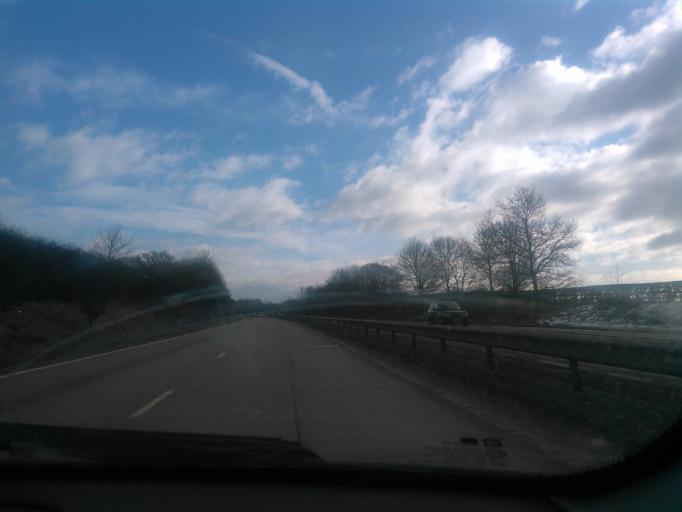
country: GB
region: England
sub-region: Staffordshire
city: Cheadle
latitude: 52.9582
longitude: -2.0486
